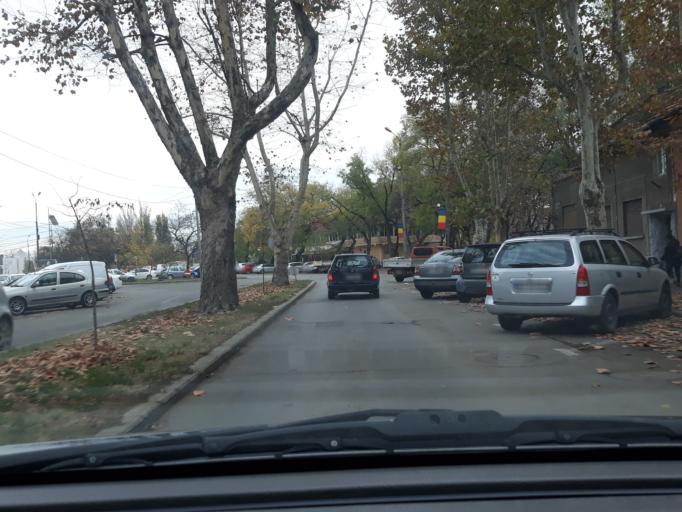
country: RO
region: Bihor
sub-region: Comuna Biharea
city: Oradea
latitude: 47.0662
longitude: 21.9212
